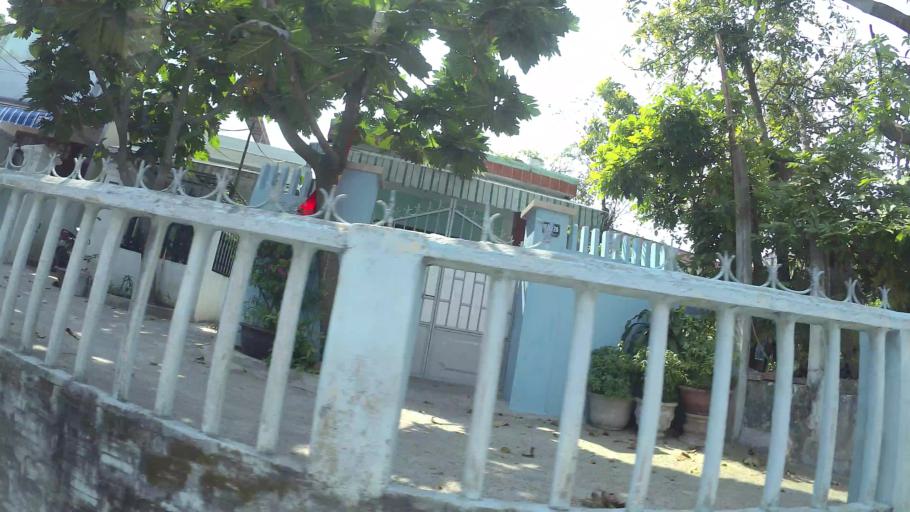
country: VN
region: Da Nang
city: Cam Le
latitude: 16.0119
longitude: 108.2018
